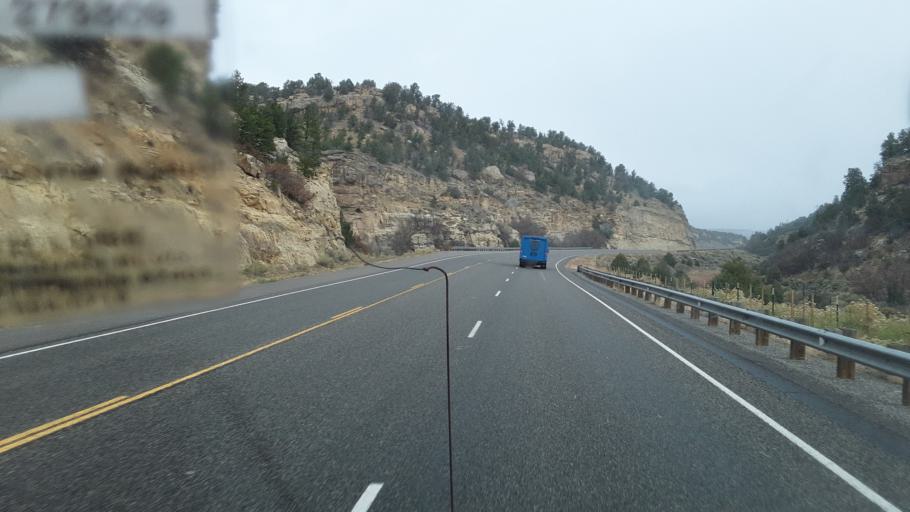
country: US
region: New Mexico
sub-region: Rio Arriba County
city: Tierra Amarilla
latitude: 36.4213
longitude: -106.4804
